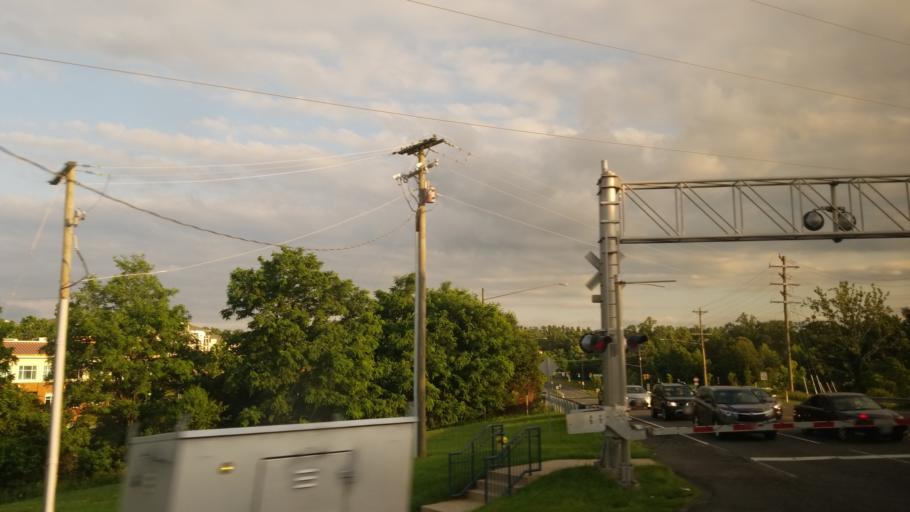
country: US
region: Virginia
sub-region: Prince William County
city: Yorkshire
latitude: 38.7646
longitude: -77.4422
